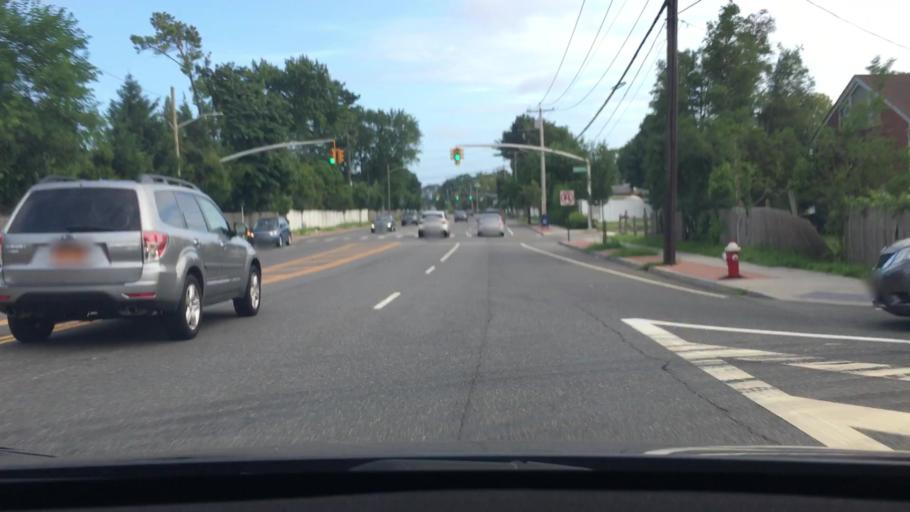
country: US
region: New York
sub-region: Nassau County
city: Hicksville
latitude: 40.7923
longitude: -73.5037
